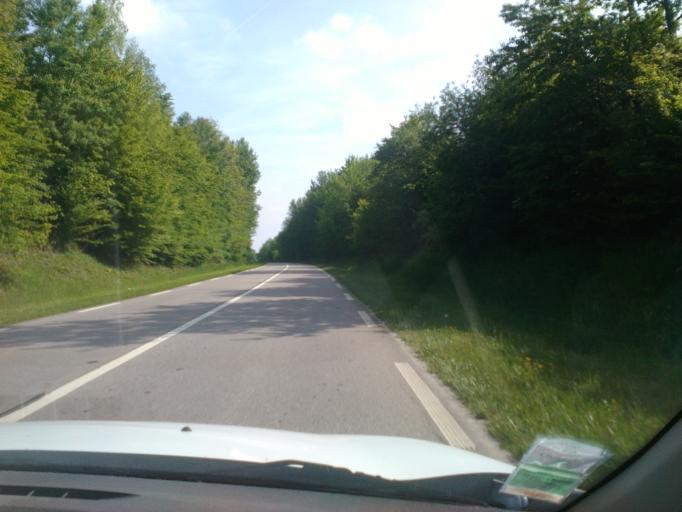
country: FR
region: Lorraine
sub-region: Departement des Vosges
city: Golbey
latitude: 48.2020
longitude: 6.4167
